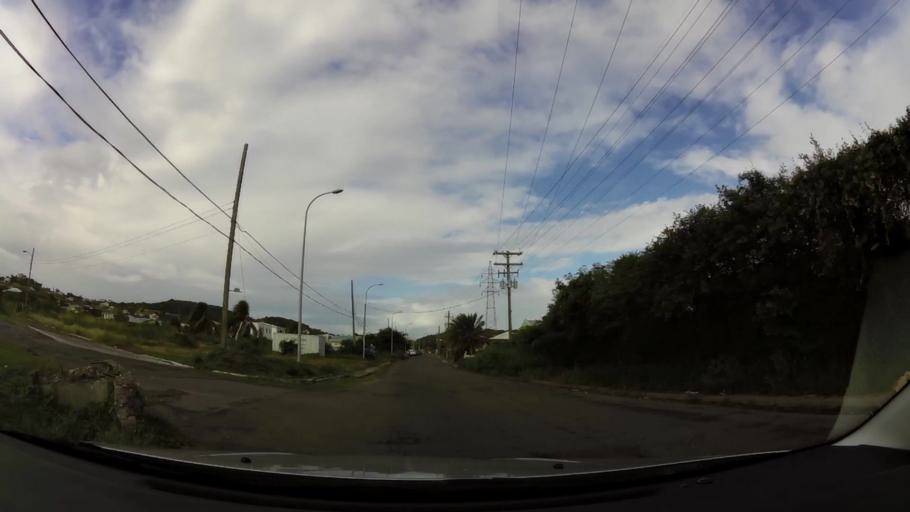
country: AG
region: Saint George
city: Piggotts
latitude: 17.1291
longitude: -61.8139
